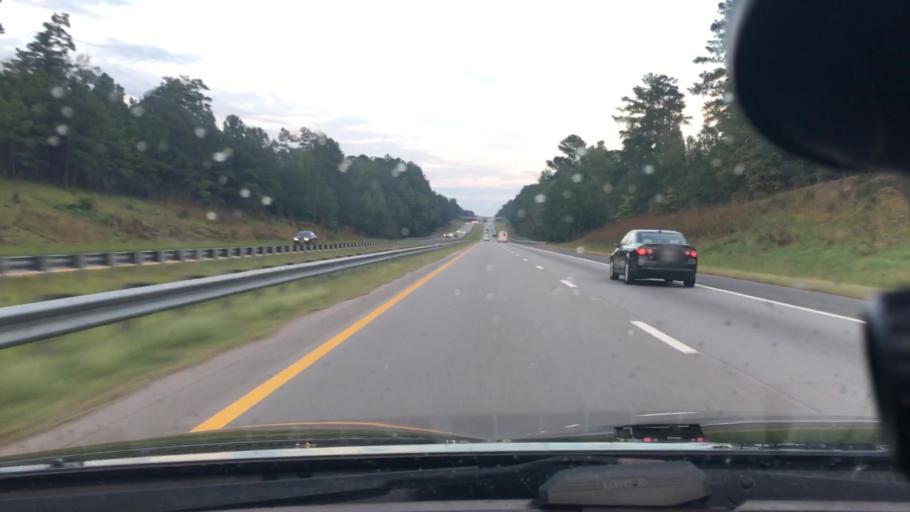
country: US
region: North Carolina
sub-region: Wake County
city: Holly Springs
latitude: 35.6559
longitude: -78.9558
